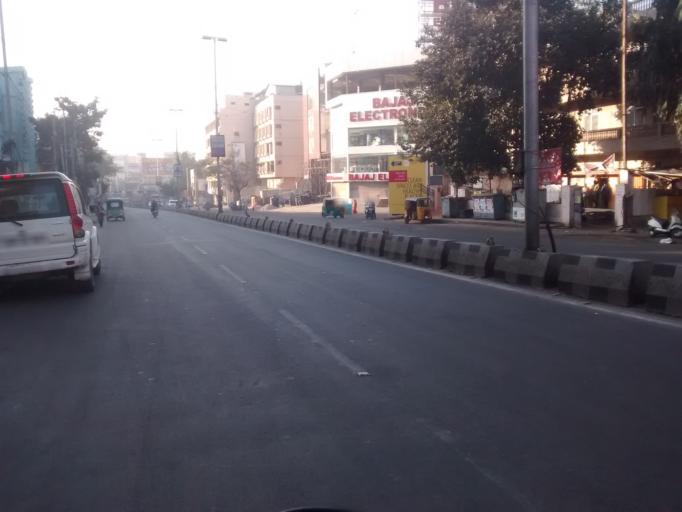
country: IN
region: Telangana
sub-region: Hyderabad
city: Malkajgiri
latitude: 17.4415
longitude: 78.4876
